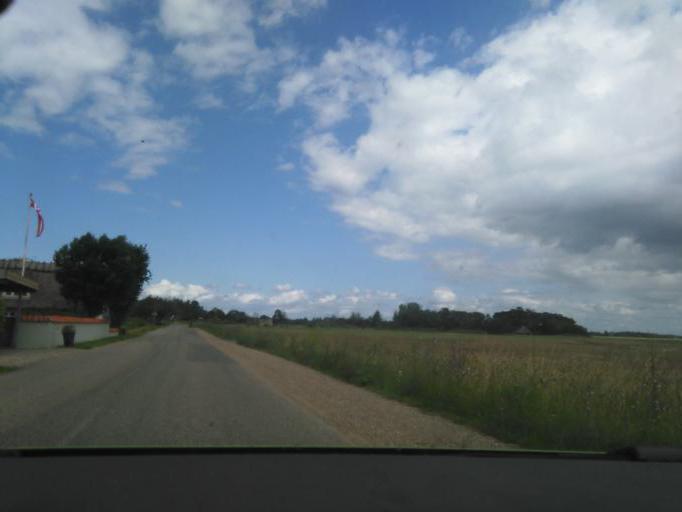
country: DK
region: Zealand
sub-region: Kalundborg Kommune
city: Gorlev
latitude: 55.5285
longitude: 11.1131
